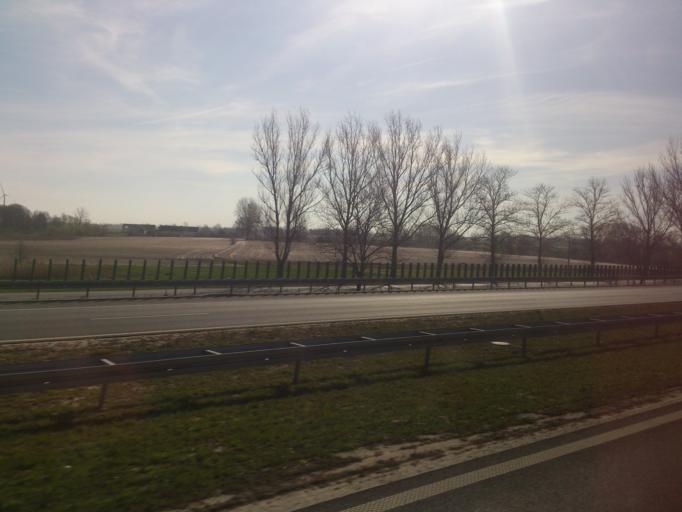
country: PL
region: Kujawsko-Pomorskie
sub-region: Powiat aleksandrowski
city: Raciazek
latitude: 52.8152
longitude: 18.8095
